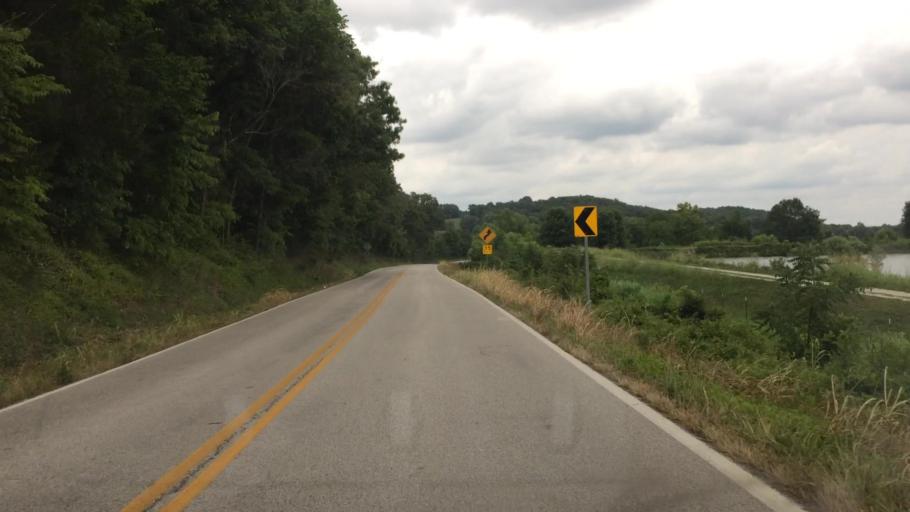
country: US
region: Missouri
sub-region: Greene County
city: Strafford
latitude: 37.2904
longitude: -93.0873
